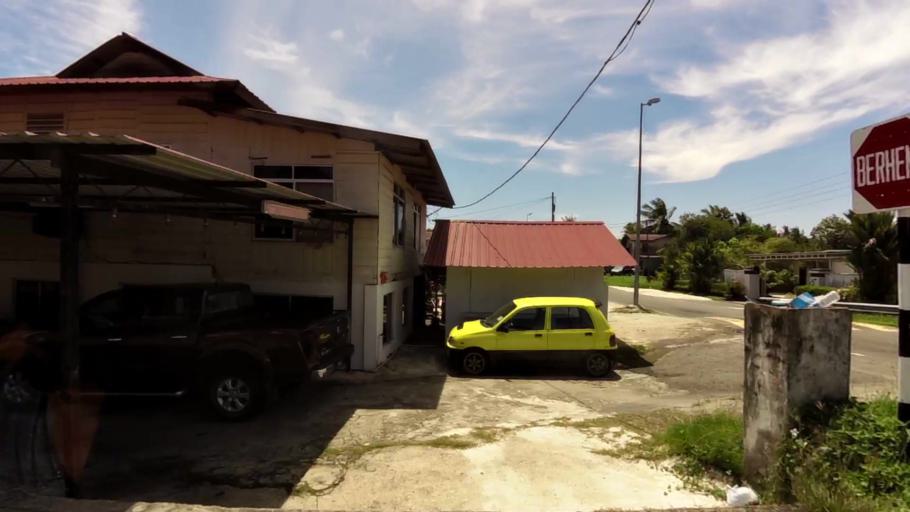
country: BN
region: Brunei and Muara
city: Bandar Seri Begawan
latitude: 4.9418
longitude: 114.9527
